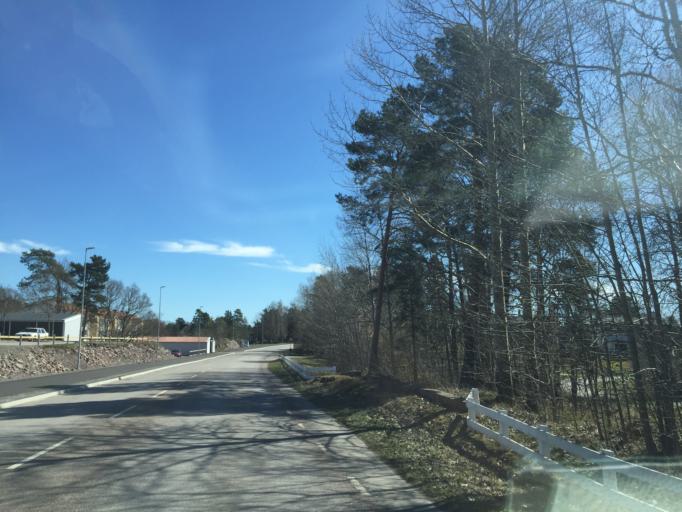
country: SE
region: Kalmar
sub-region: Oskarshamns Kommun
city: Oskarshamn
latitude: 57.2469
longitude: 16.4663
